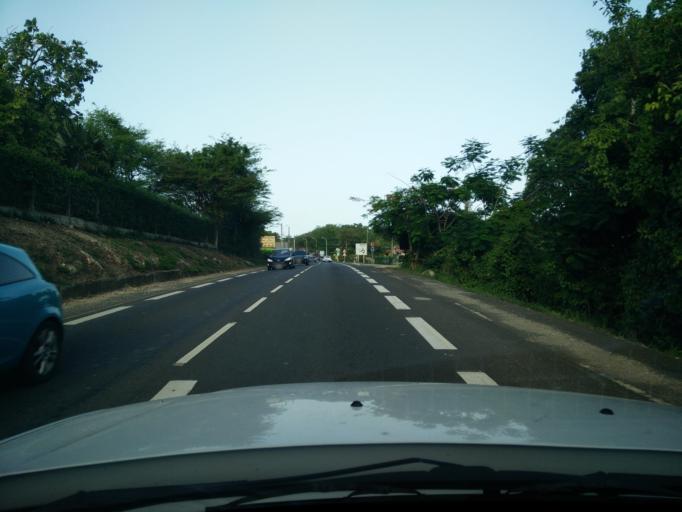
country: GP
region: Guadeloupe
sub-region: Guadeloupe
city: Le Gosier
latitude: 16.2079
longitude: -61.4636
